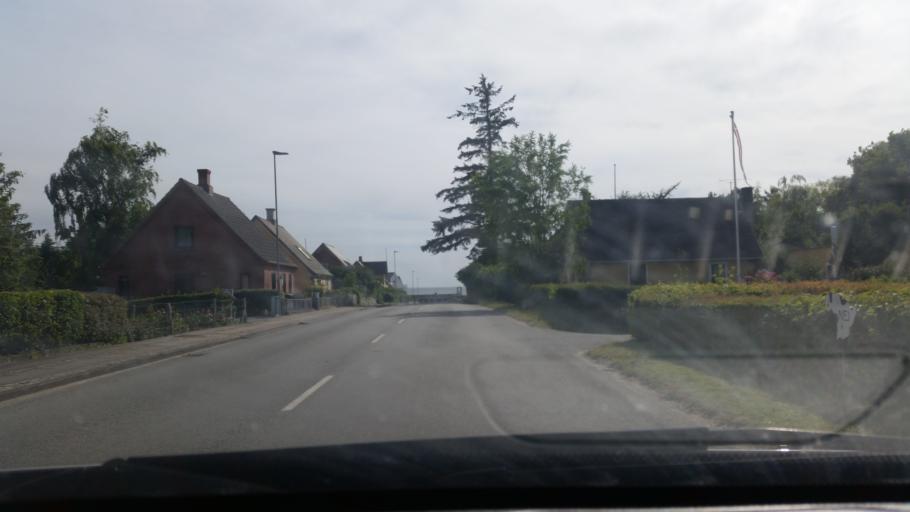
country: DK
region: Central Jutland
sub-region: Samso Kommune
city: Tranebjerg
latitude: 55.7987
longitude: 10.5331
